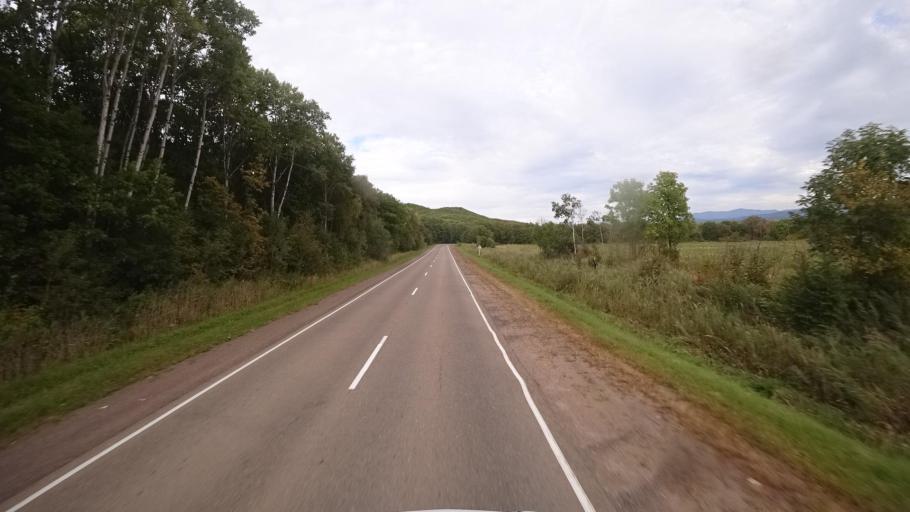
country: RU
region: Primorskiy
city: Yakovlevka
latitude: 44.3766
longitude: 133.4441
